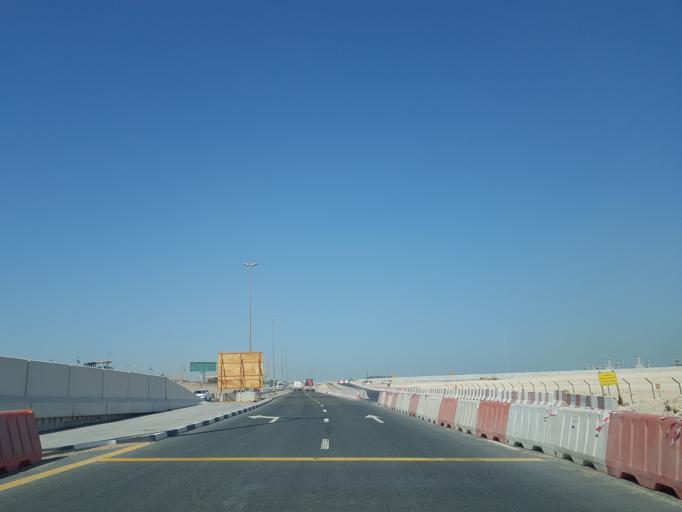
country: AE
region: Dubai
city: Dubai
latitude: 25.0143
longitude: 55.0906
